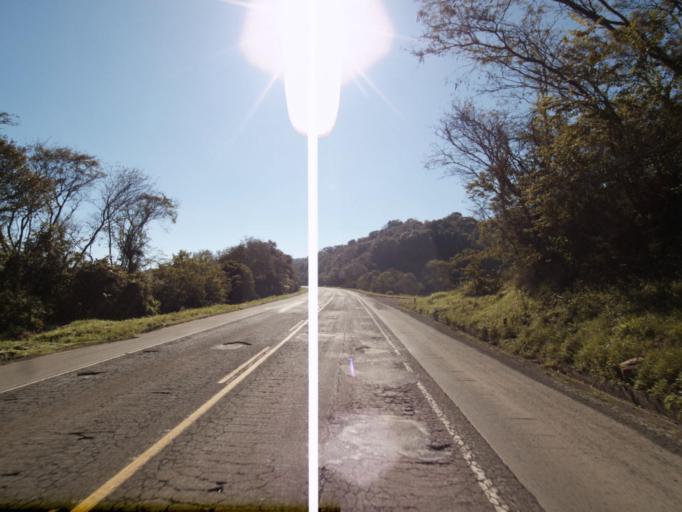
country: BR
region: Rio Grande do Sul
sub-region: Frederico Westphalen
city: Frederico Westphalen
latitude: -27.0132
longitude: -53.2259
